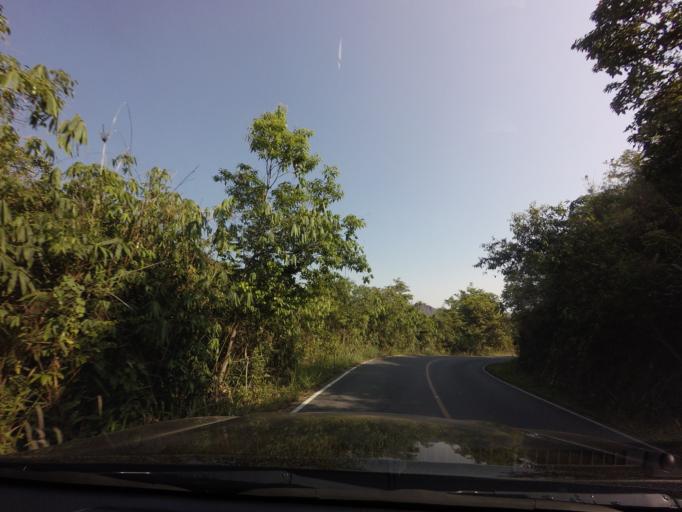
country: TH
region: Kanchanaburi
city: Thong Pha Phum
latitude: 14.6761
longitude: 98.3758
